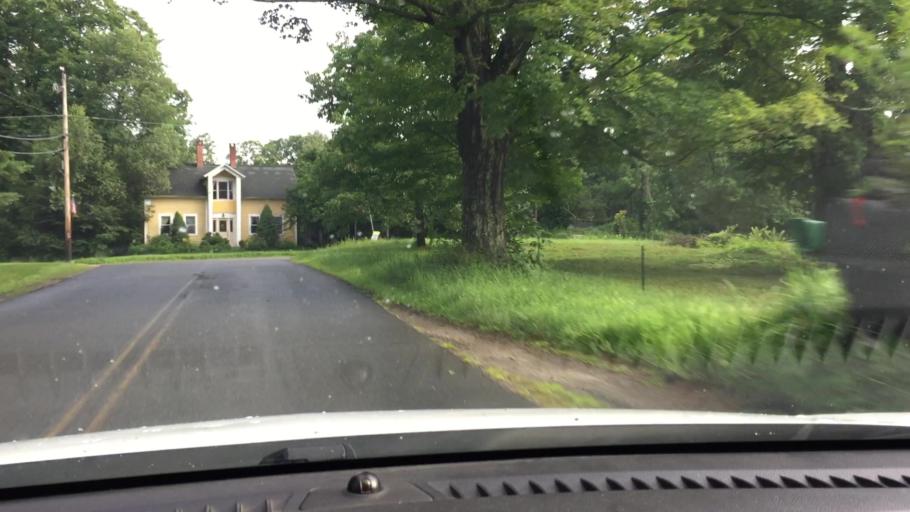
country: US
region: Massachusetts
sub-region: Berkshire County
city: Becket
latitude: 42.4230
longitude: -72.9864
